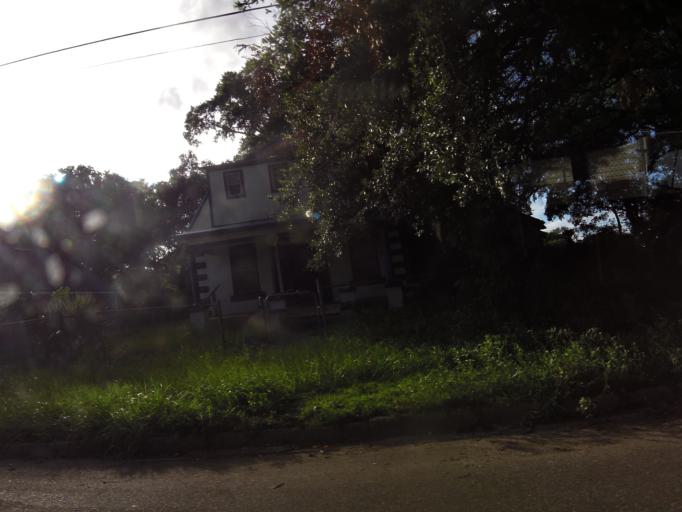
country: US
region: Florida
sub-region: Duval County
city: Jacksonville
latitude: 30.3756
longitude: -81.6657
